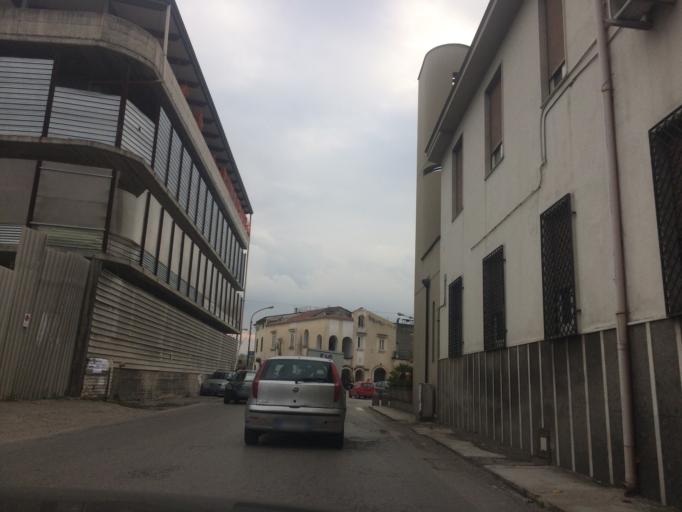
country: IT
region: Campania
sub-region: Provincia di Napoli
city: Piazzolla
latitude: 40.8800
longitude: 14.5287
